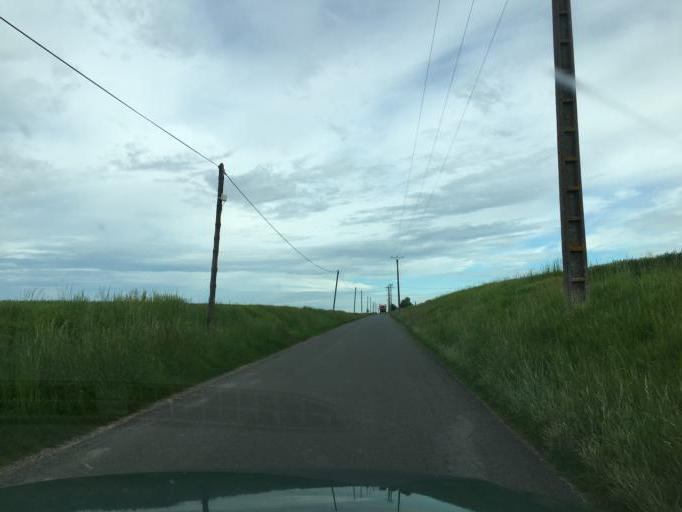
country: FR
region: Centre
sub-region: Departement du Loiret
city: Bricy
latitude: 47.9641
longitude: 1.7506
